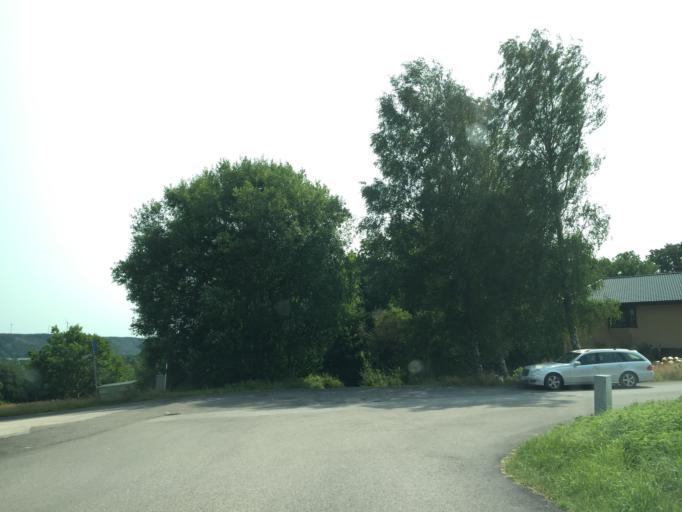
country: SE
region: Vaestra Goetaland
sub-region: Lilla Edets Kommun
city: Lilla Edet
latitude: 58.1788
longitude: 12.1085
